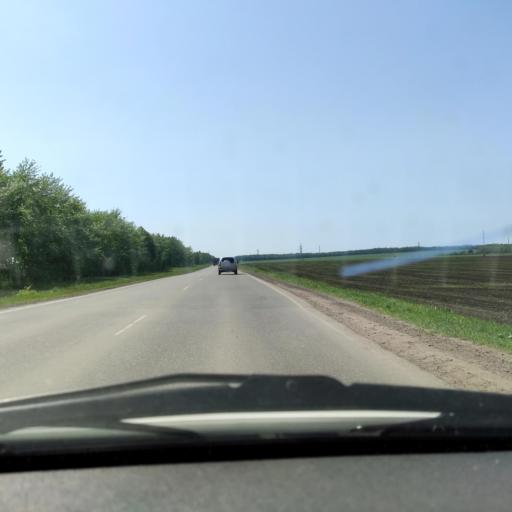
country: RU
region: Bashkortostan
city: Avdon
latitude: 54.5814
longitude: 55.7793
